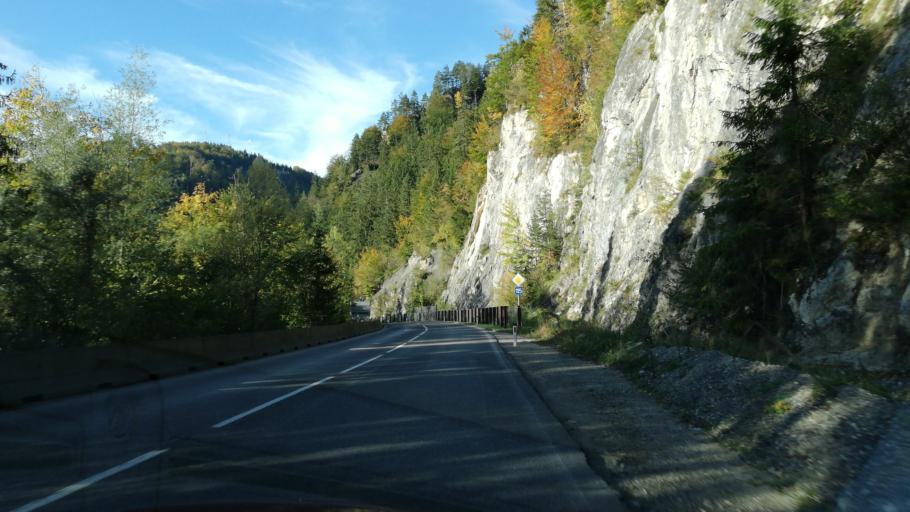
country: AT
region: Styria
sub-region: Politischer Bezirk Liezen
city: Altenmarkt bei Sankt Gallen
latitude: 47.7259
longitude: 14.6502
